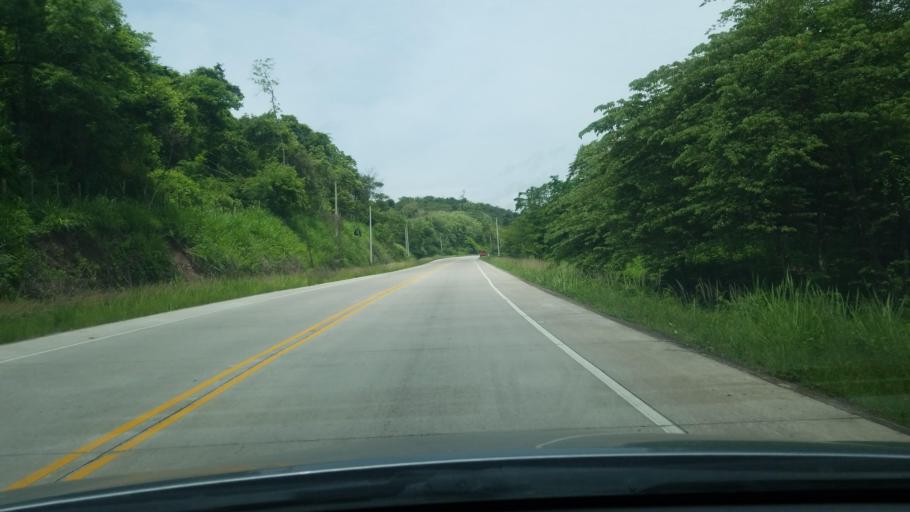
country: HN
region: Copan
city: Quezailica
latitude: 14.8907
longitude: -88.7636
